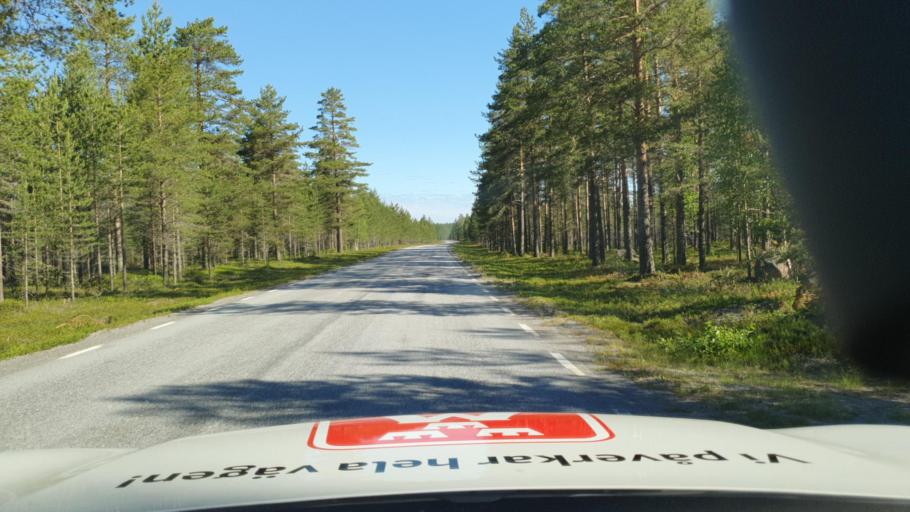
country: SE
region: Vaesterbotten
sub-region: Umea Kommun
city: Roback
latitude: 63.8806
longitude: 20.1513
